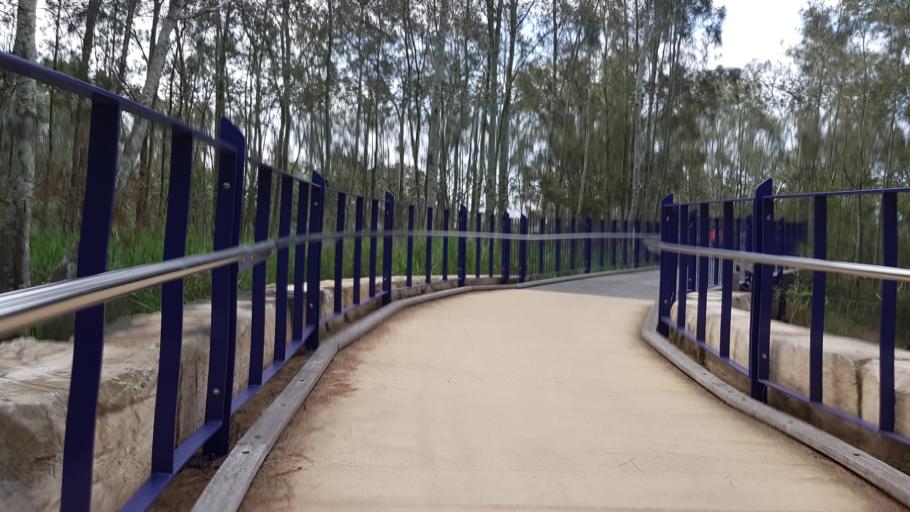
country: AU
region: New South Wales
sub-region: Warringah
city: Narrabeen
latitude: -33.7236
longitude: 151.2743
